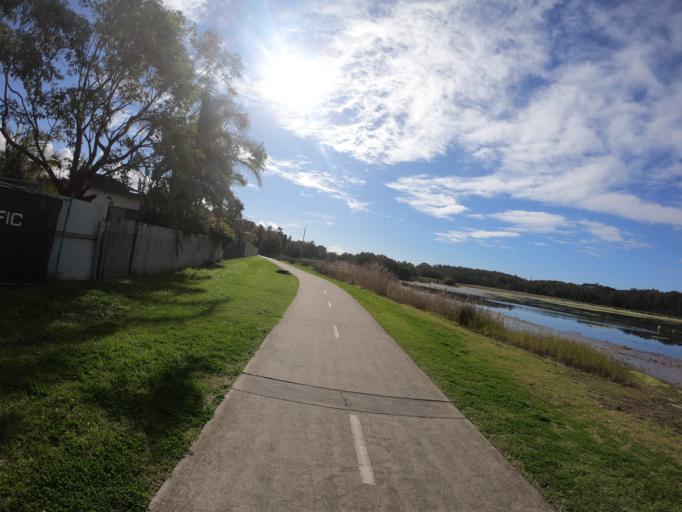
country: AU
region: New South Wales
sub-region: Wollongong
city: East Corrimal
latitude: -34.3732
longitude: 150.9196
